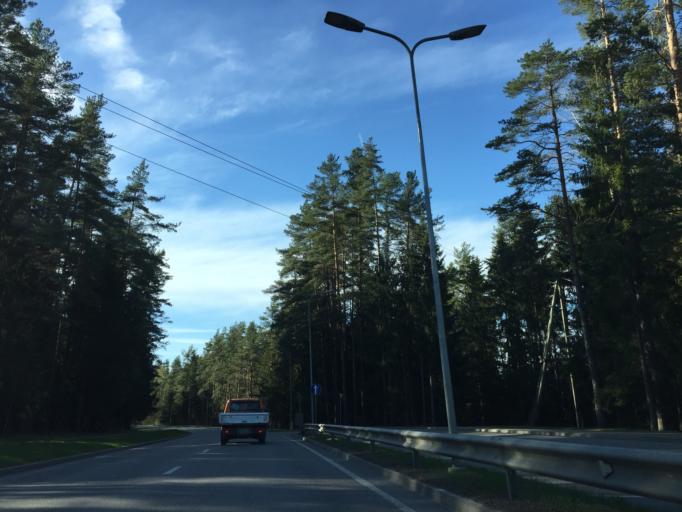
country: LV
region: Valkas Rajons
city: Valka
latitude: 57.7838
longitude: 26.0025
